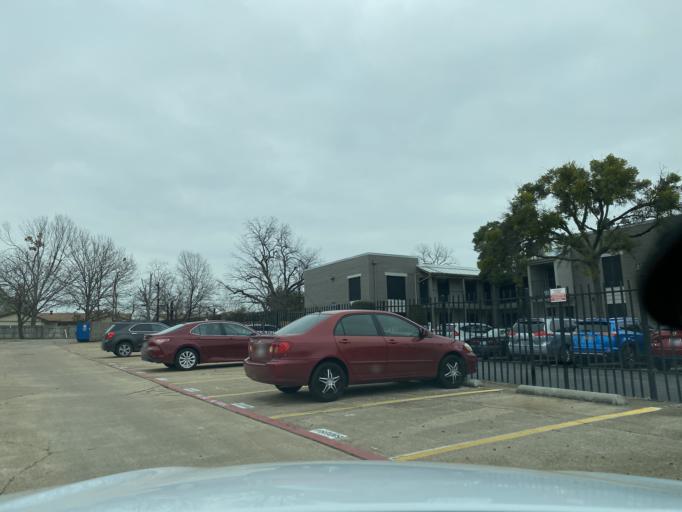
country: US
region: Texas
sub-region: Tarrant County
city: Euless
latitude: 32.8271
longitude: -97.0961
